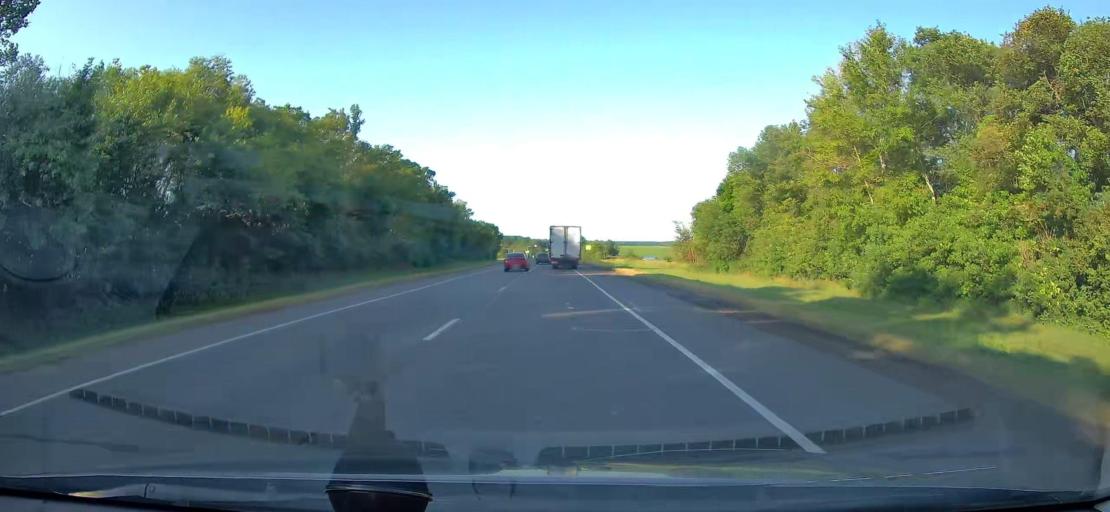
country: RU
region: Tula
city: Plavsk
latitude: 53.6269
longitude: 37.1984
